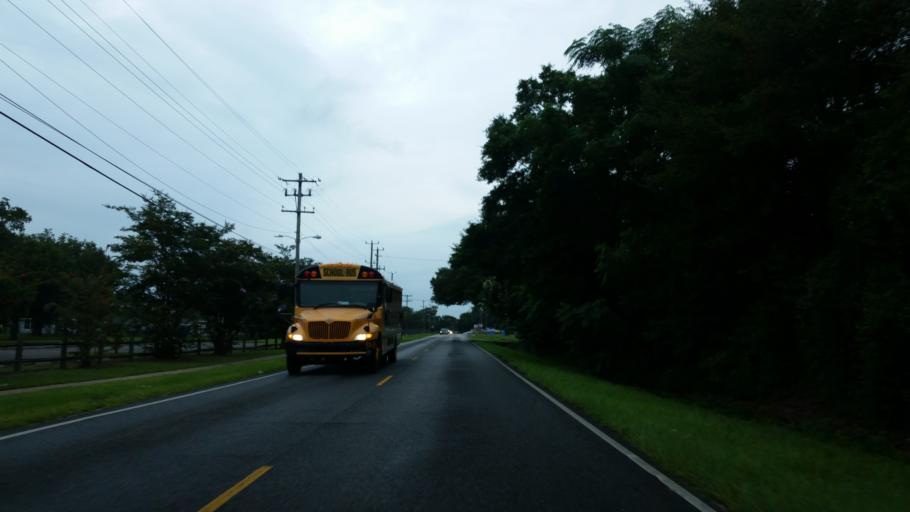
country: US
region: Florida
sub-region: Escambia County
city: Warrington
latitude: 30.3976
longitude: -87.2736
